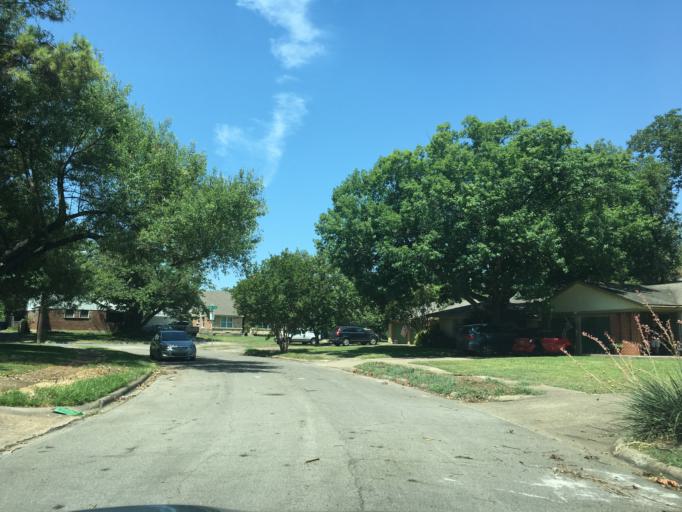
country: US
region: Texas
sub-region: Dallas County
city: Highland Park
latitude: 32.8510
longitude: -96.7410
